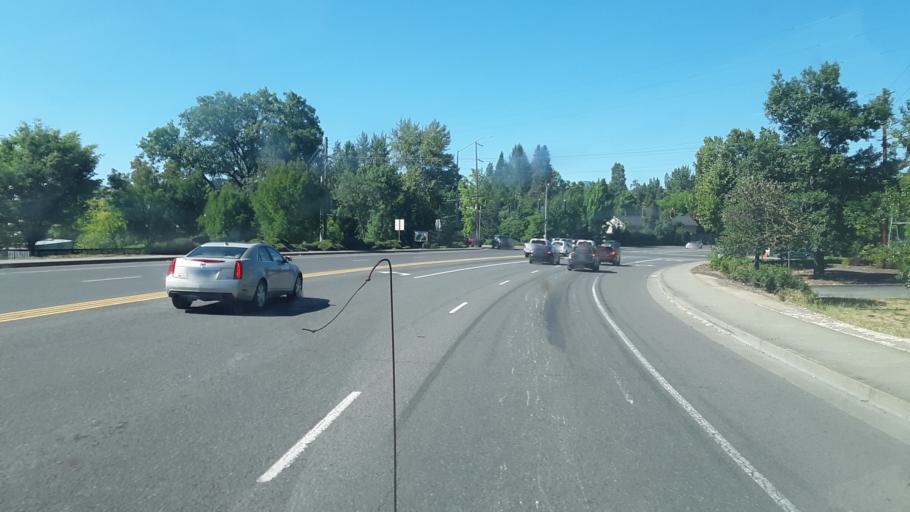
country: US
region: Oregon
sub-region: Josephine County
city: Fruitdale
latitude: 42.4281
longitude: -123.3191
